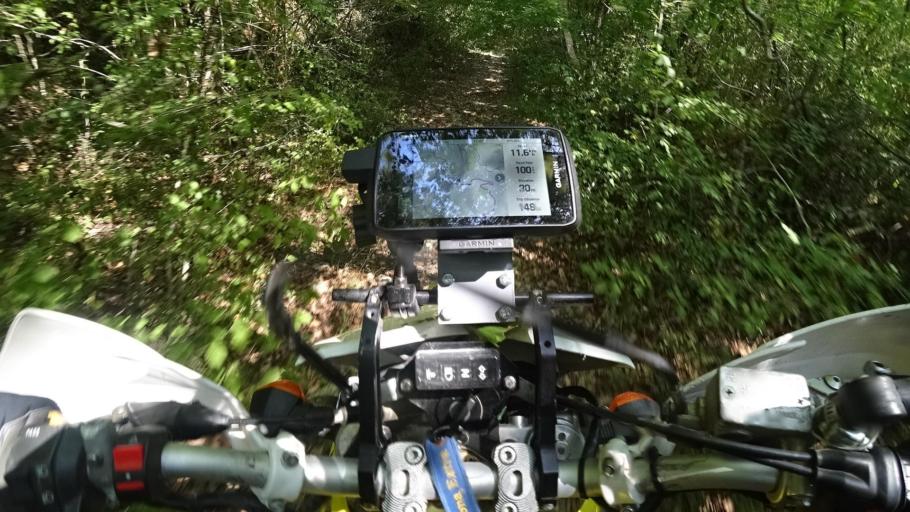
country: HR
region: Istarska
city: Pazin
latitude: 45.2966
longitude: 13.9308
